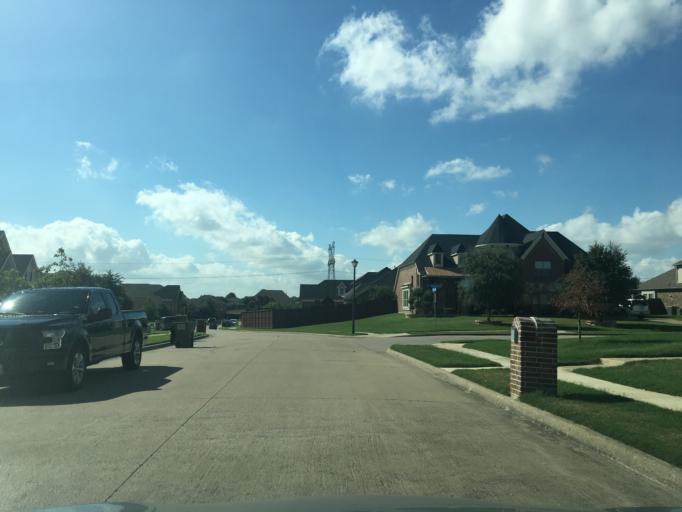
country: US
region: Texas
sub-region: Dallas County
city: Sachse
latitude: 32.9699
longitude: -96.5778
